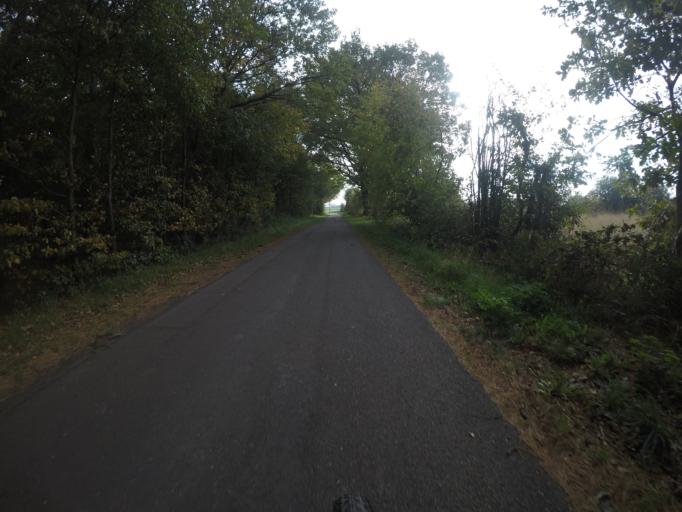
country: DE
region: North Rhine-Westphalia
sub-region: Regierungsbezirk Munster
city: Isselburg
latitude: 51.8327
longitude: 6.4988
